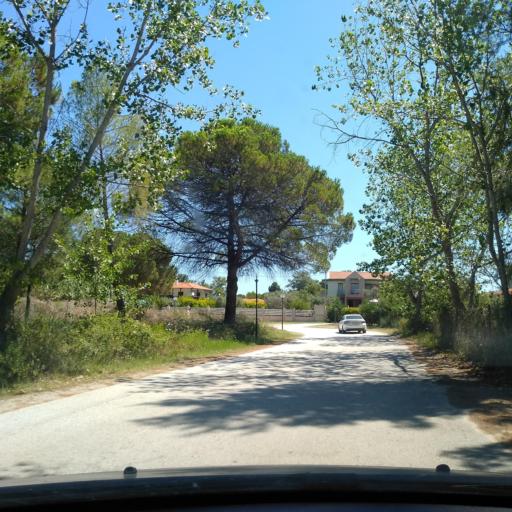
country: GR
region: Central Macedonia
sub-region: Nomos Chalkidikis
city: Neos Marmaras
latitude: 40.1890
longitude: 23.8060
